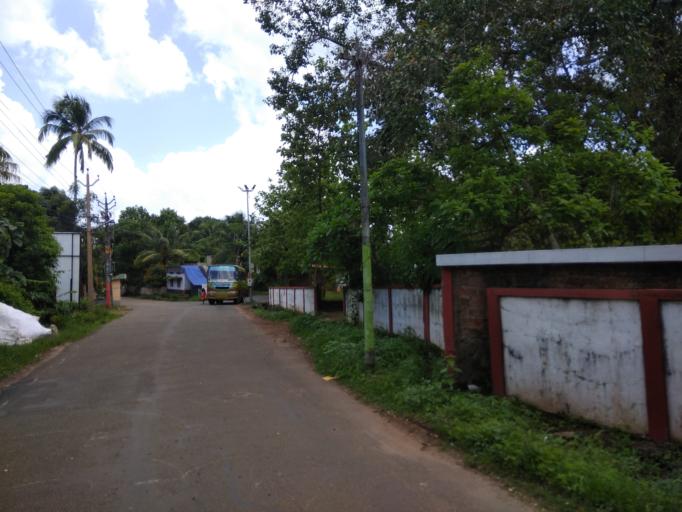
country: IN
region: Kerala
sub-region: Thrissur District
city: Avanoor
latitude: 10.5427
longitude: 76.1434
